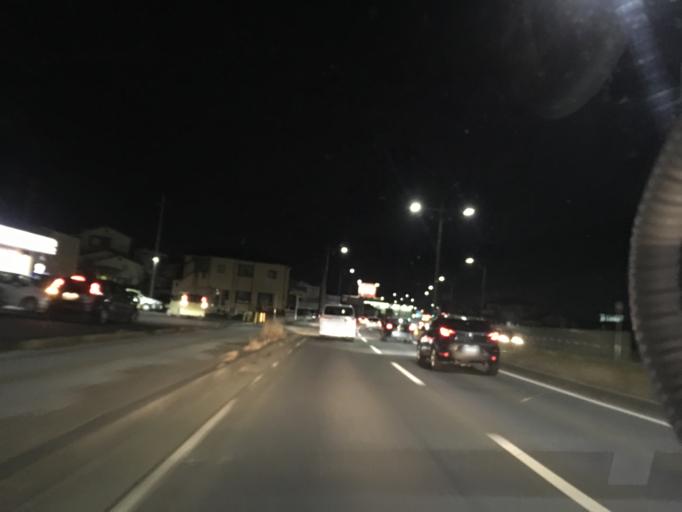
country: JP
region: Miyagi
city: Ishinomaki
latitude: 38.4433
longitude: 141.2761
